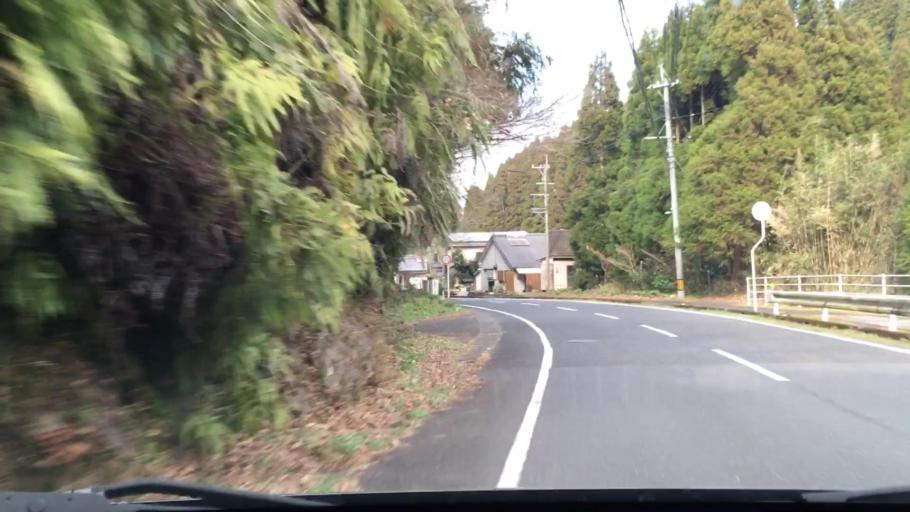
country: JP
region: Miyazaki
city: Kushima
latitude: 31.5439
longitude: 131.2420
